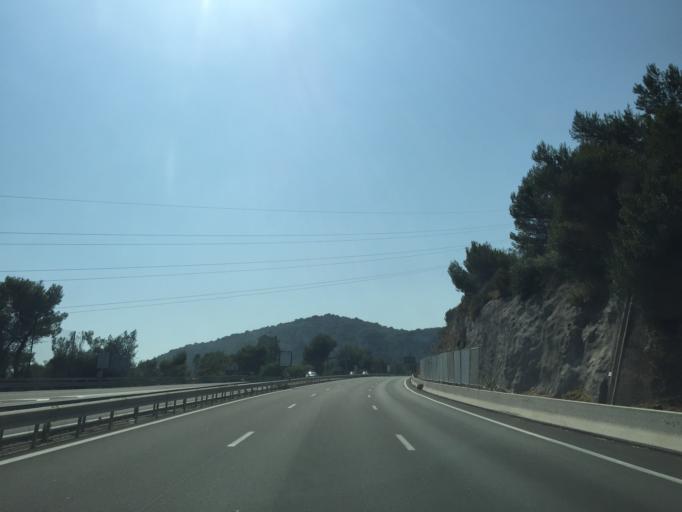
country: FR
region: Provence-Alpes-Cote d'Azur
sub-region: Departement des Alpes-Maritimes
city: Beausoleil
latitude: 43.7516
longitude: 7.4120
